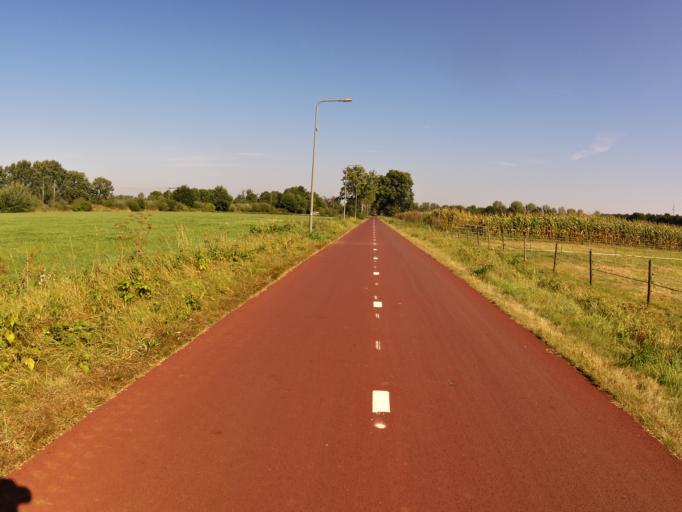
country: NL
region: North Brabant
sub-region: Gemeente Maasdonk
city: Geffen
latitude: 51.7504
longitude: 5.4835
